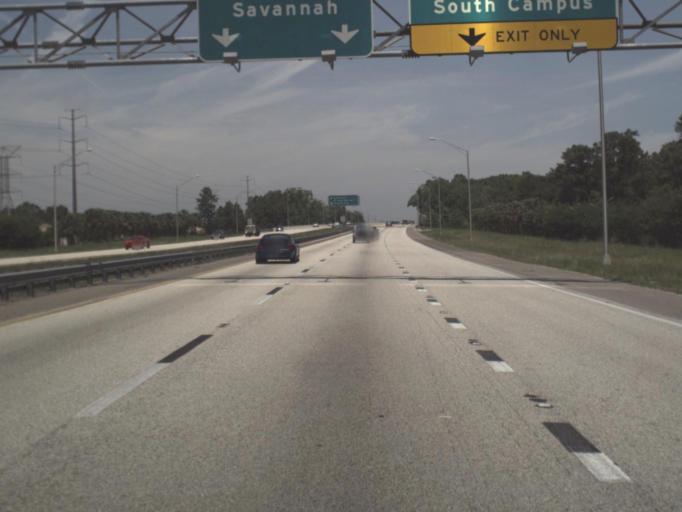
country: US
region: Florida
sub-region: Duval County
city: Jacksonville Beach
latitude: 30.2736
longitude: -81.5212
